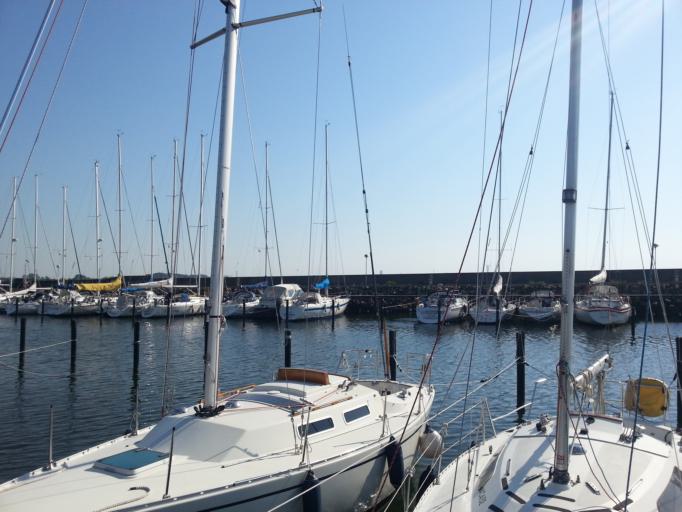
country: SE
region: Skane
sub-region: Lomma Kommun
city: Lomma
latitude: 55.6748
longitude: 13.0588
